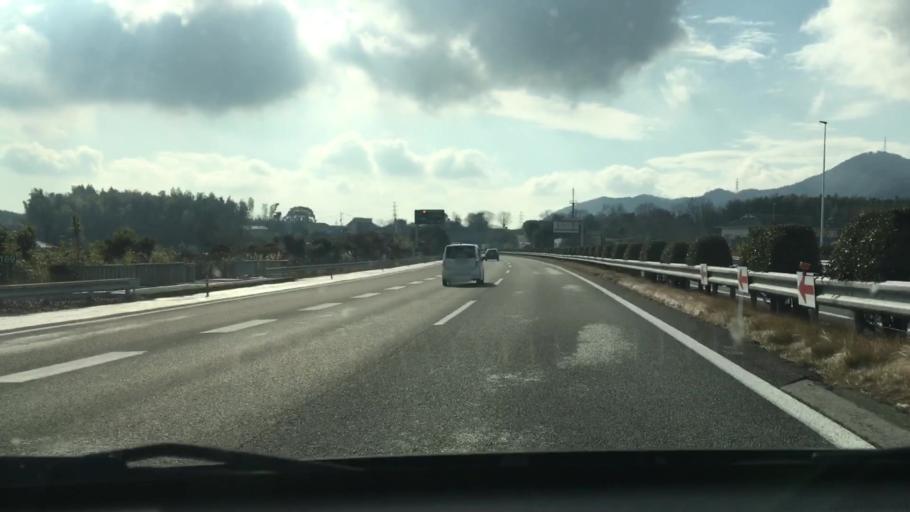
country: JP
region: Kumamoto
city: Uto
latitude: 32.6936
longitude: 130.7410
